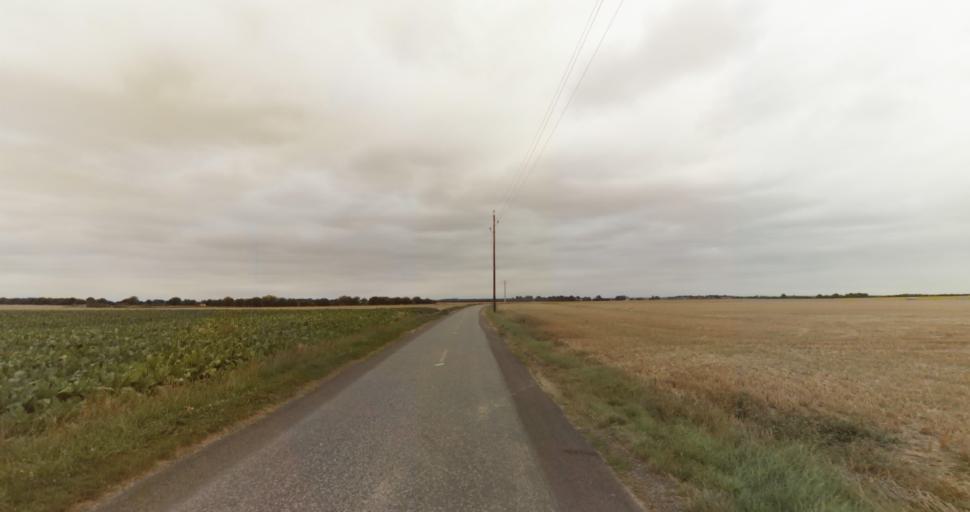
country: FR
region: Haute-Normandie
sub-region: Departement de l'Eure
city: La Couture-Boussey
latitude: 48.9220
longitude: 1.3065
